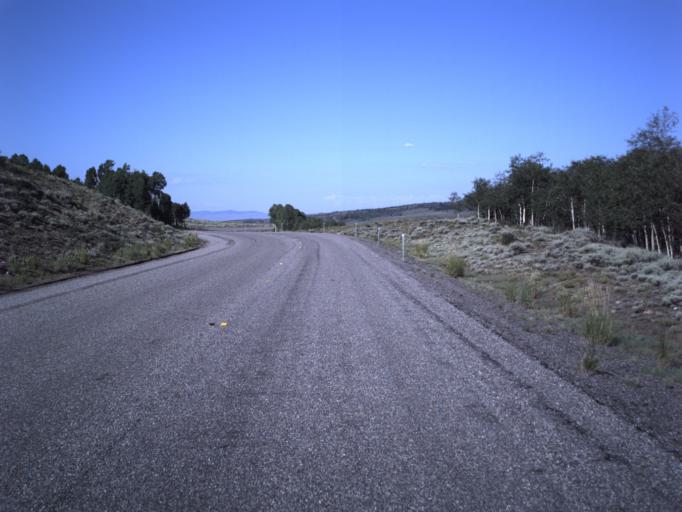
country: US
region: Utah
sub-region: Wayne County
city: Loa
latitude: 38.5779
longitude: -111.4871
